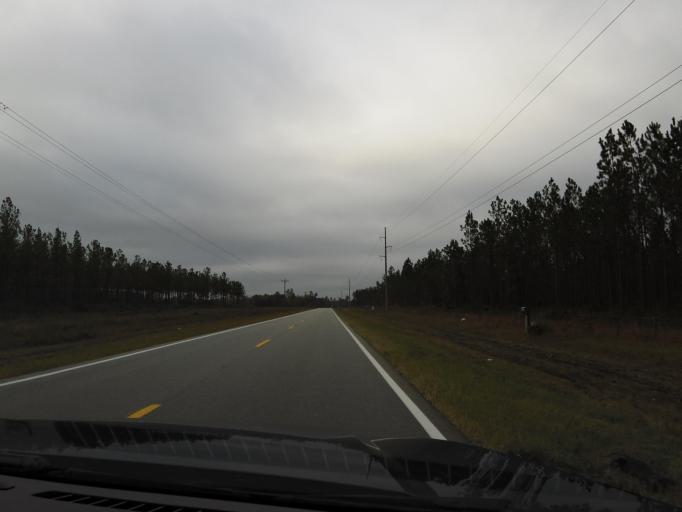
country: US
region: Georgia
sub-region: Charlton County
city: Folkston
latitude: 30.7511
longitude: -82.0706
